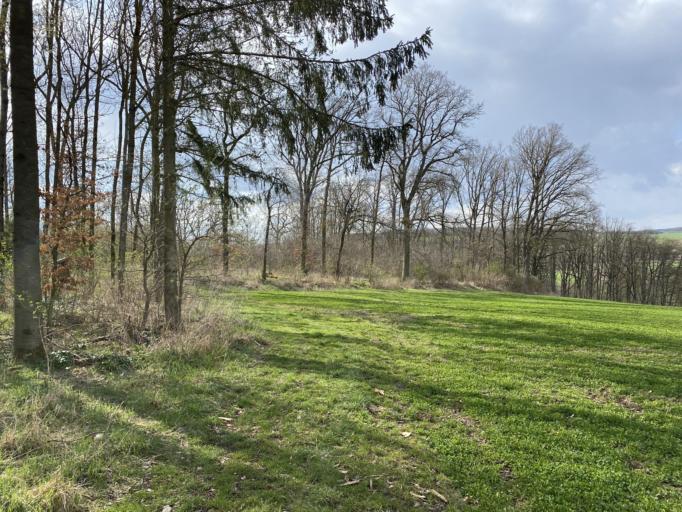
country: DE
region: Bavaria
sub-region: Regierungsbezirk Unterfranken
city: Werneck
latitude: 49.9627
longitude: 10.0659
